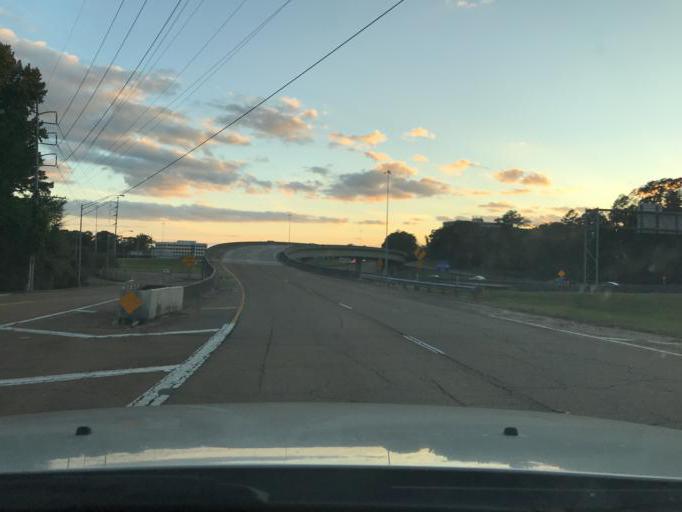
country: US
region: Mississippi
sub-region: Rankin County
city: Flowood
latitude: 32.3517
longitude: -90.1521
